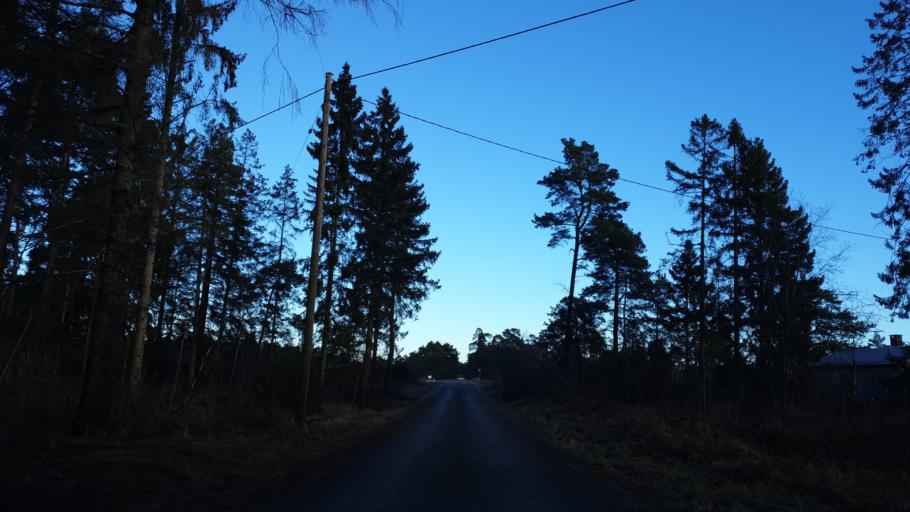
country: SE
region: Gotland
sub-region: Gotland
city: Slite
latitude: 57.3785
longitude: 18.8039
